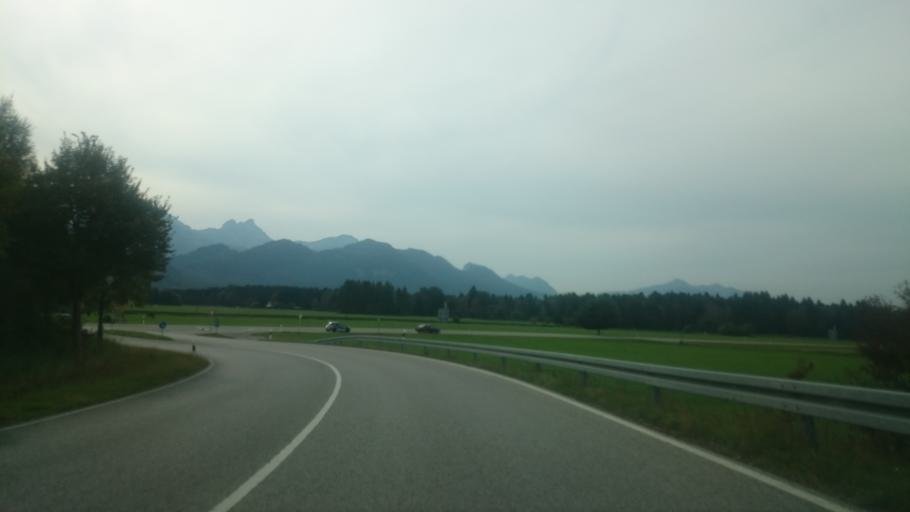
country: DE
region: Bavaria
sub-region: Swabia
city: Fuessen
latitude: 47.5804
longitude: 10.6778
